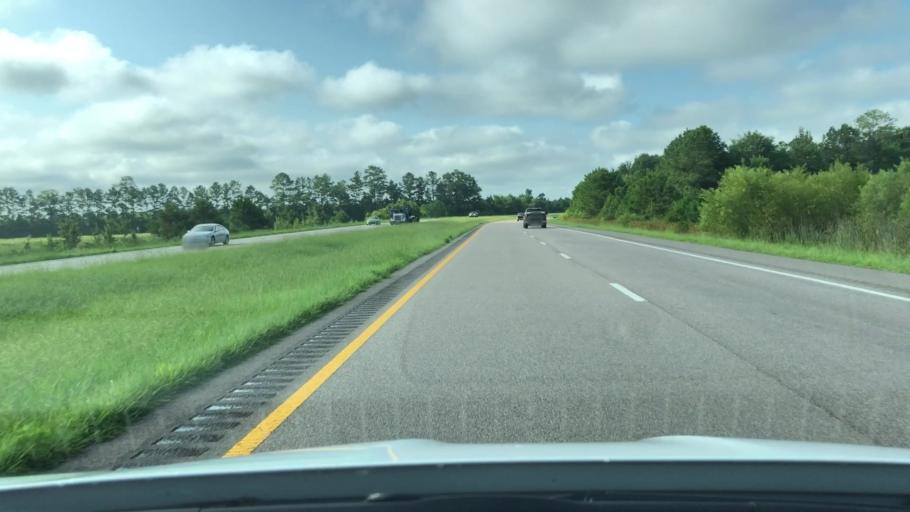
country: US
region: Virginia
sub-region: City of Portsmouth
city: Portsmouth Heights
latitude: 36.6811
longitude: -76.3473
